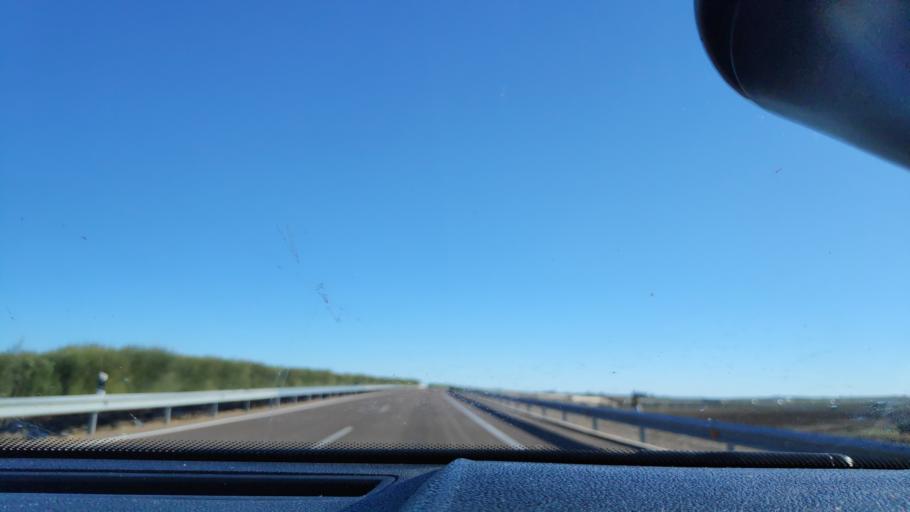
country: ES
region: Extremadura
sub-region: Provincia de Badajoz
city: Villafranca de los Barros
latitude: 38.5319
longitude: -6.3551
